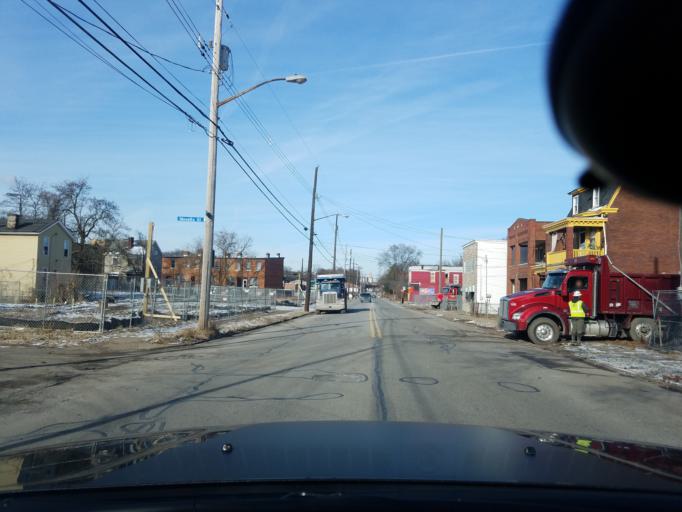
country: US
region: Pennsylvania
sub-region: Allegheny County
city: Wilkinsburg
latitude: 40.4554
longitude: -79.9008
